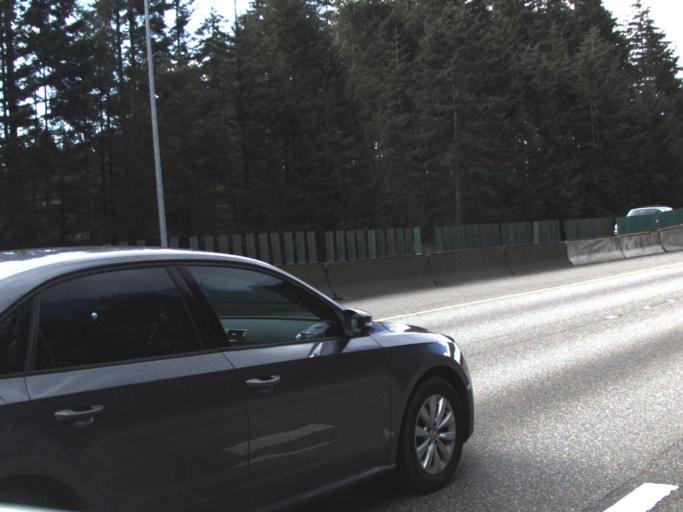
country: US
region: Washington
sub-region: King County
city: Lakeland South
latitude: 47.2973
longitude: -122.2865
